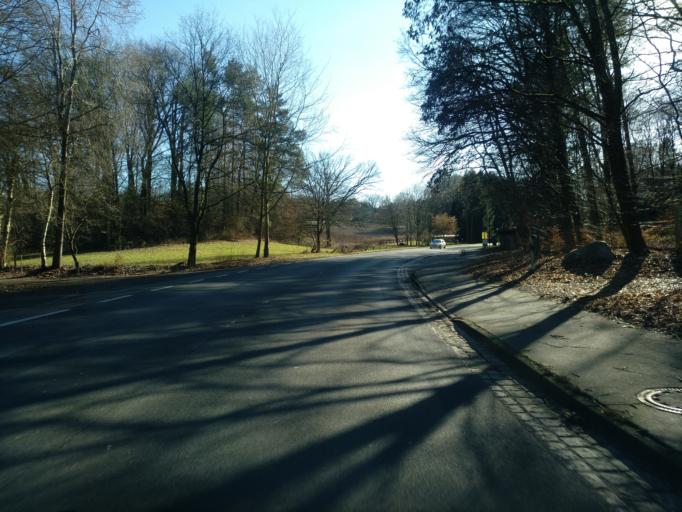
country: DE
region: Hamburg
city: Harburg
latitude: 53.4516
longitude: 9.9055
